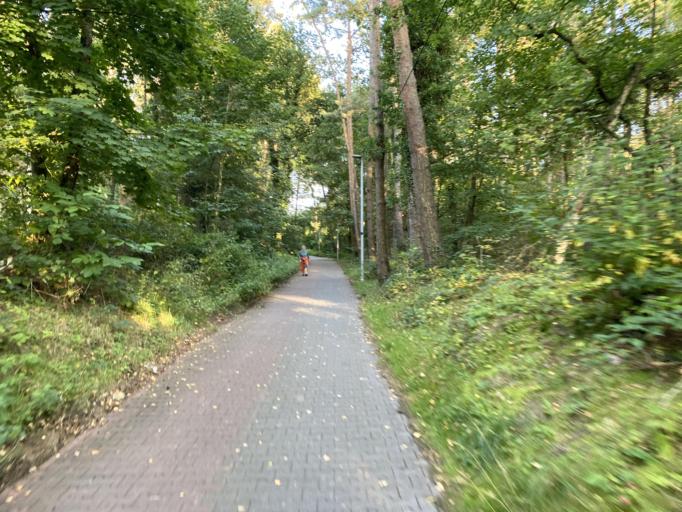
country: DE
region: North Rhine-Westphalia
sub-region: Regierungsbezirk Detmold
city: Lage
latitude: 51.9453
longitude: 8.8170
